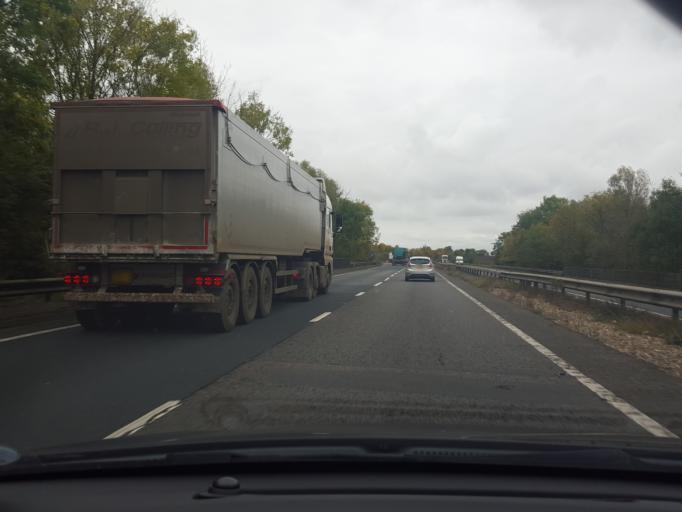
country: GB
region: England
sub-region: Suffolk
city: Needham Market
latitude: 52.1698
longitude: 1.0539
